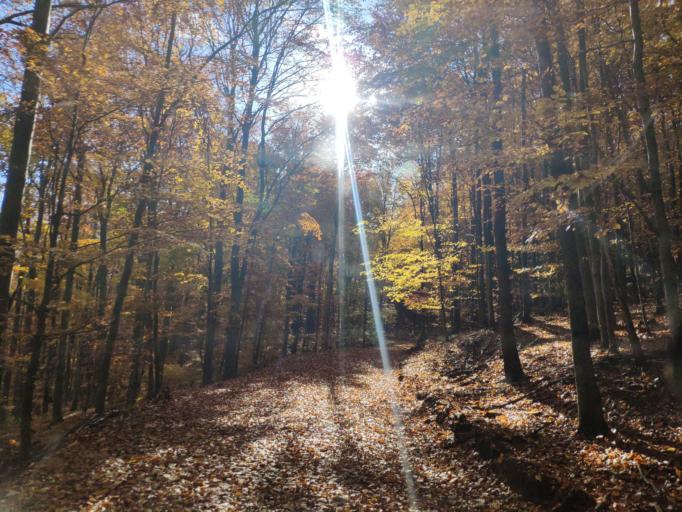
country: SK
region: Kosicky
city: Moldava nad Bodvou
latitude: 48.7276
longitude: 21.0310
